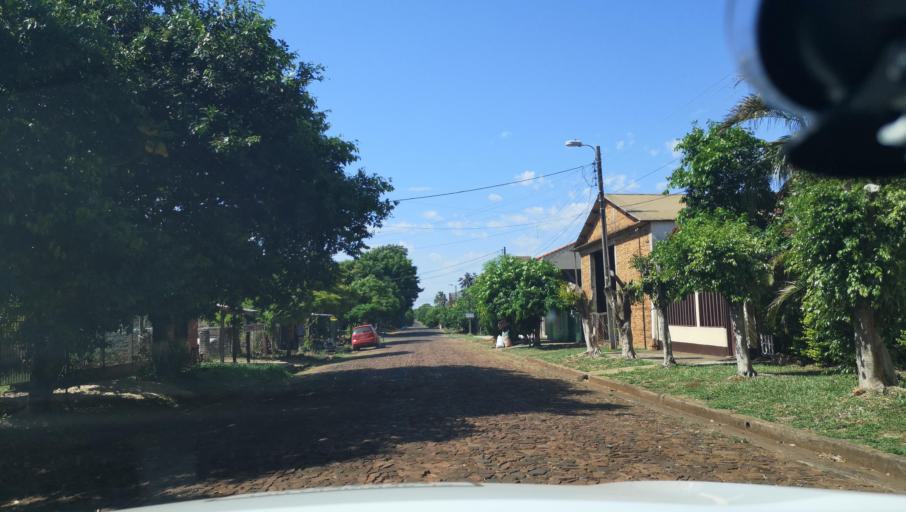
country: PY
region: Itapua
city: Carmen del Parana
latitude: -27.1559
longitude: -56.2346
